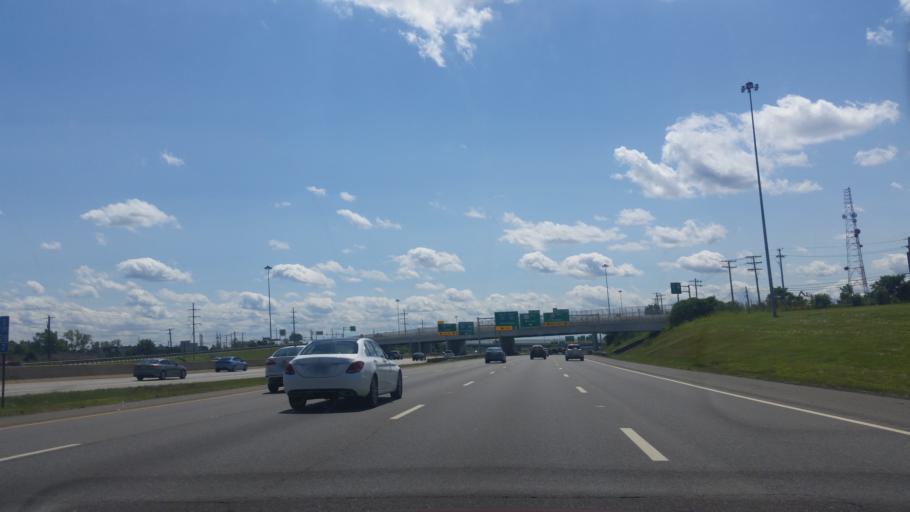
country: US
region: Ohio
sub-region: Cuyahoga County
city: Orange
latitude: 41.4401
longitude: -81.4965
